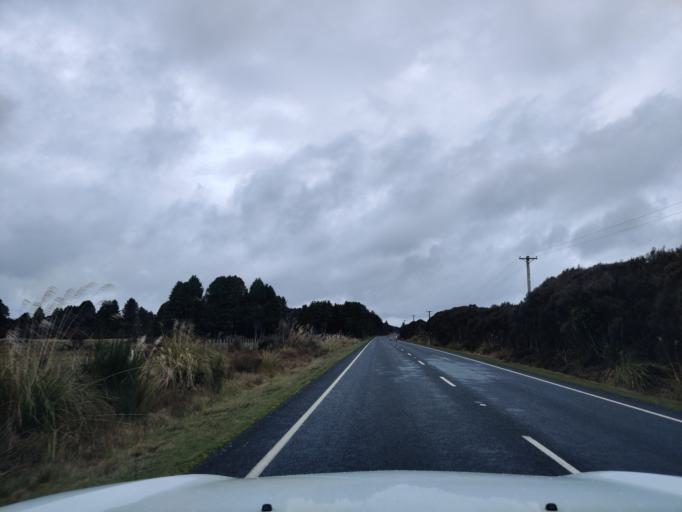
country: NZ
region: Manawatu-Wanganui
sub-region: Ruapehu District
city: Waiouru
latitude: -39.3372
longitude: 175.3795
